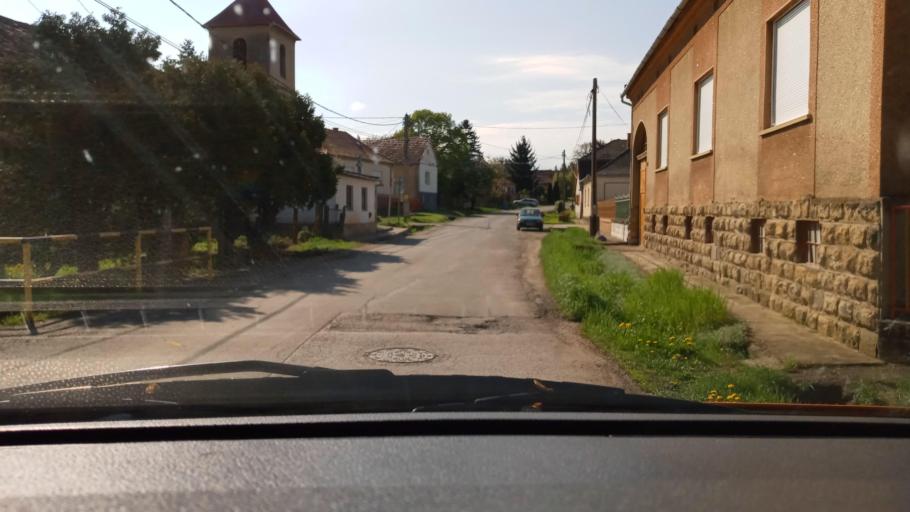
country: HU
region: Baranya
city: Hosszuheteny
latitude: 46.1083
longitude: 18.3429
